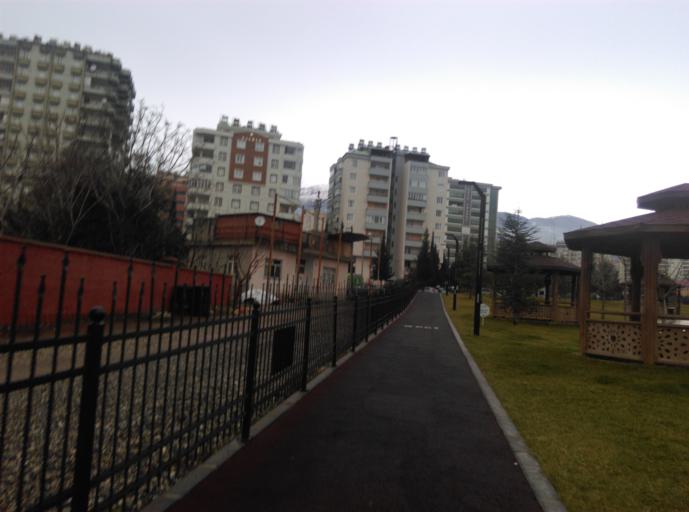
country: TR
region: Kahramanmaras
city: Kahramanmaras
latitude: 37.5825
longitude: 36.8892
